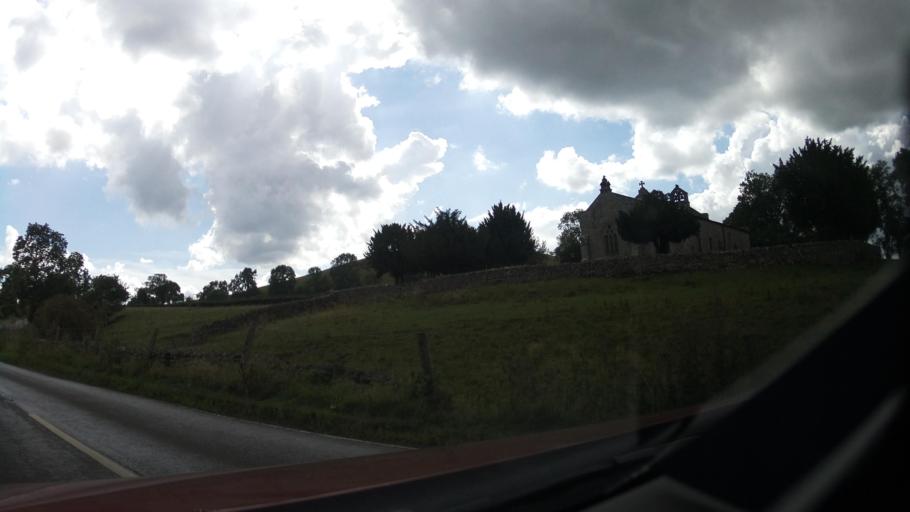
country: GB
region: England
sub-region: North Yorkshire
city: Leyburn
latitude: 54.3810
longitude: -1.8303
